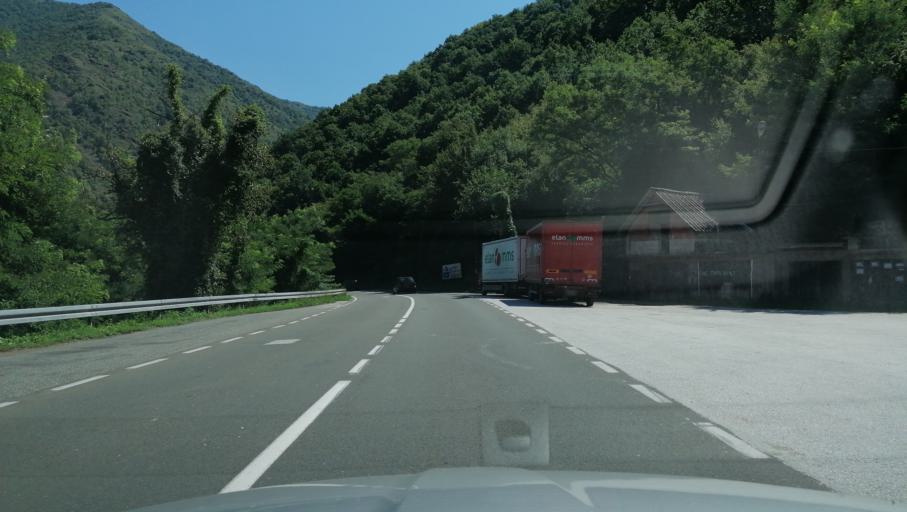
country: RS
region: Central Serbia
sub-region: Raski Okrug
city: Kraljevo
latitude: 43.6114
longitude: 20.5491
